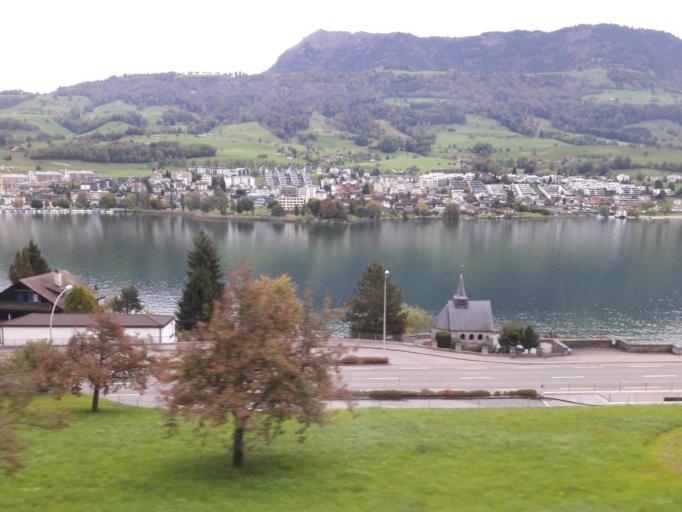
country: CH
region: Schwyz
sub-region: Bezirk Kuessnacht
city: Kussnacht
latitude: 47.0793
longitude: 8.4300
